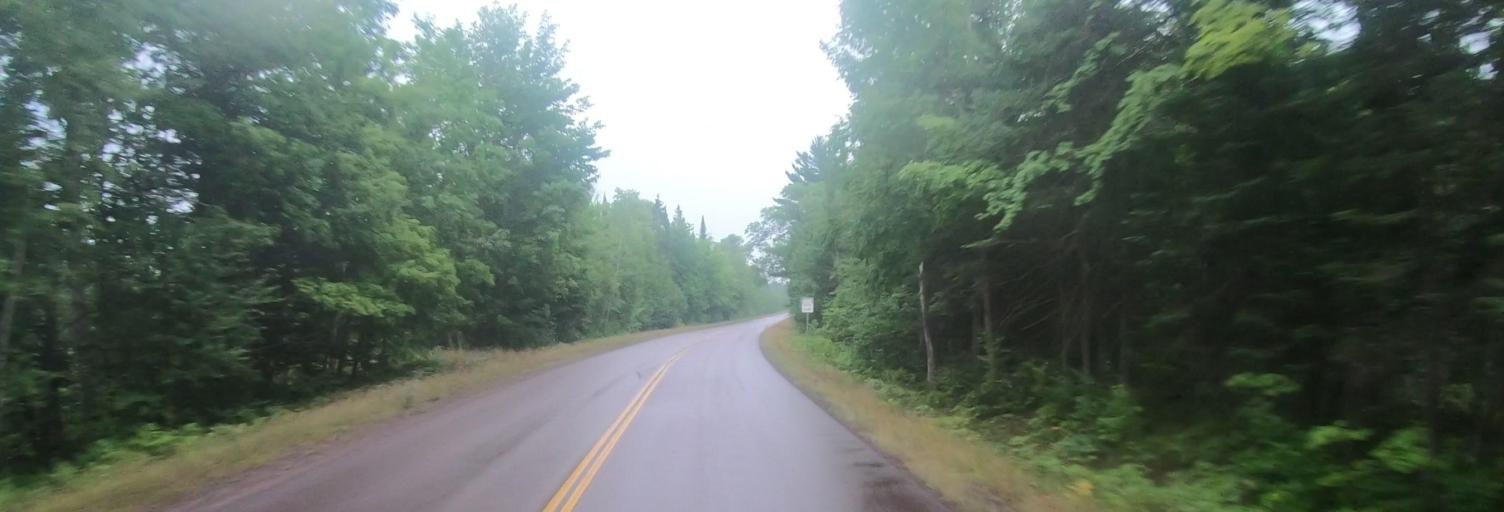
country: US
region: Michigan
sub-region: Keweenaw County
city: Eagle River
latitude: 47.2783
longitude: -88.2686
